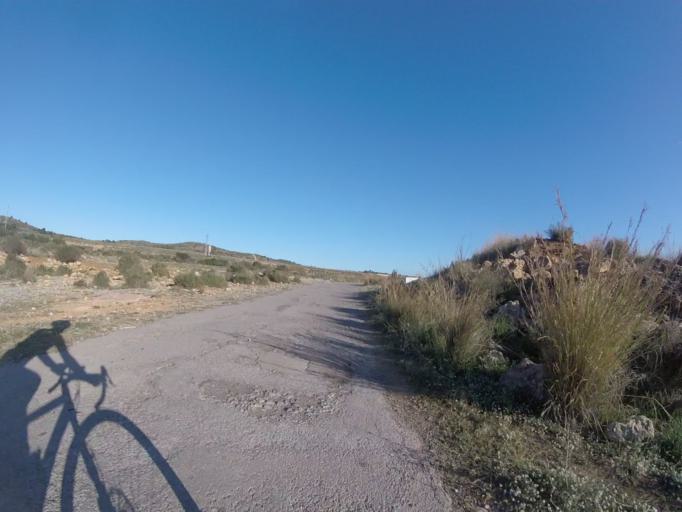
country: ES
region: Valencia
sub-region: Provincia de Castello
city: Torreblanca
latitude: 40.2289
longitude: 0.2009
